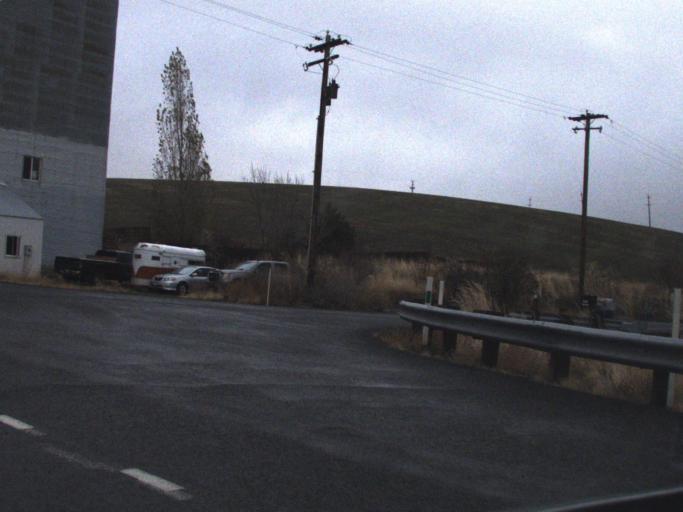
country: US
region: Washington
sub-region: Walla Walla County
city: Waitsburg
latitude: 46.1655
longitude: -118.1307
